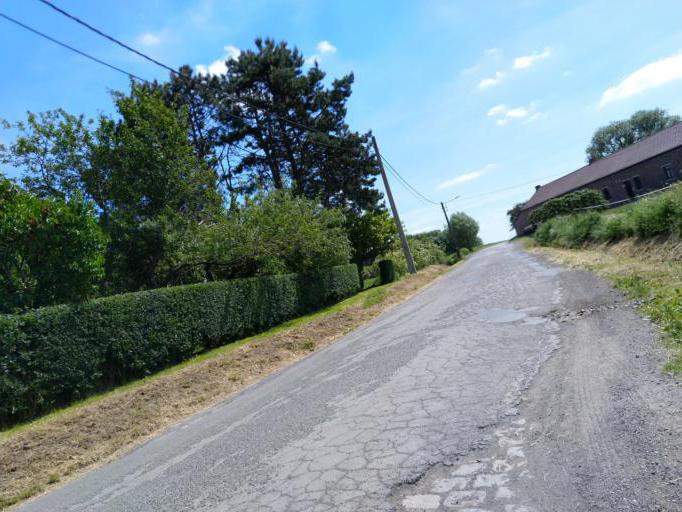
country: BE
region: Wallonia
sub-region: Province du Hainaut
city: Roeulx
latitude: 50.5071
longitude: 4.0497
